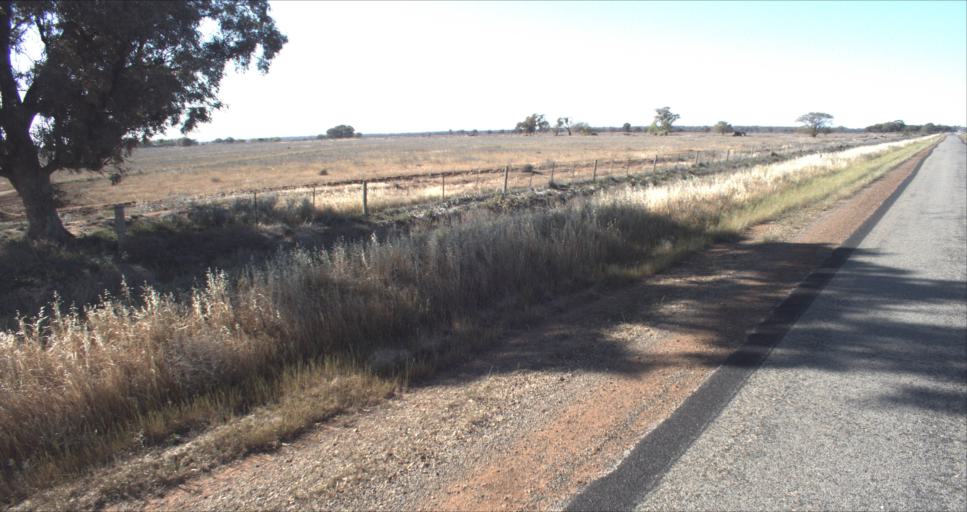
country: AU
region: New South Wales
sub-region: Leeton
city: Leeton
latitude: -34.5799
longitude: 146.2618
